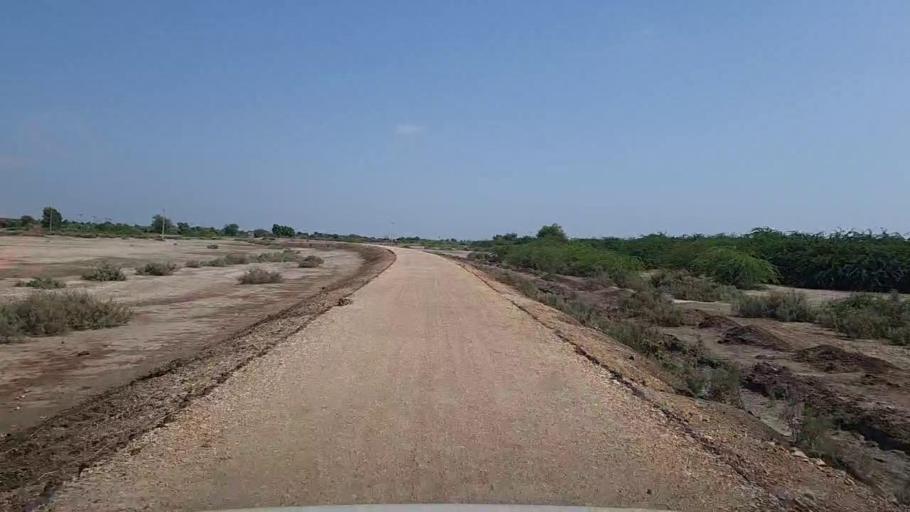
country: PK
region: Sindh
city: Talhar
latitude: 24.8355
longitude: 68.7181
